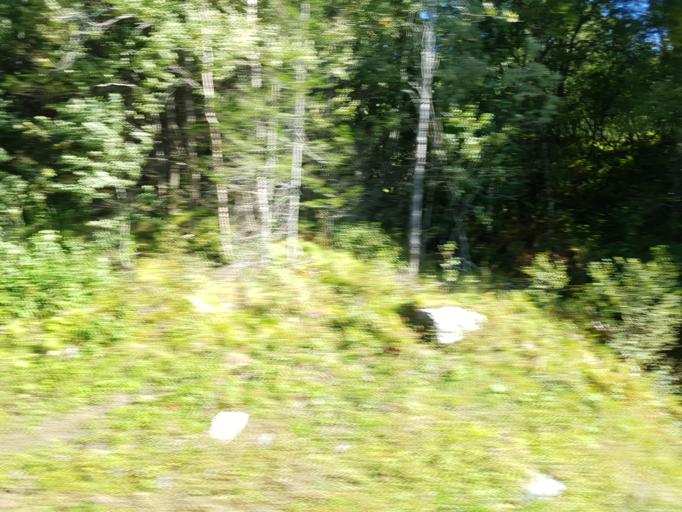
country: NO
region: Sor-Trondelag
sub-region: Afjord
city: A i Afjord
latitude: 63.7448
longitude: 10.2380
